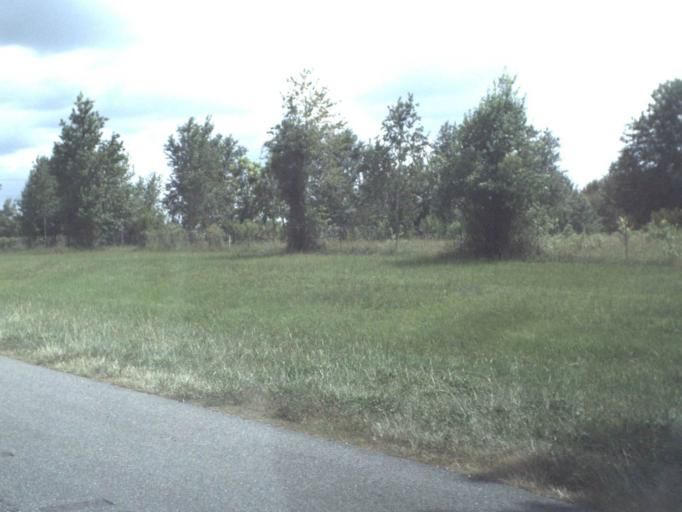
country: US
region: Florida
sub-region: Columbia County
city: Lake City
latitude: 30.0554
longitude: -82.6237
